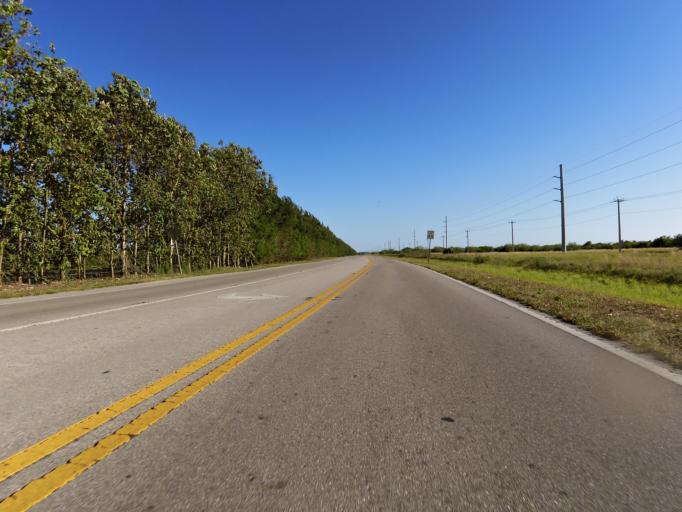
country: US
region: Florida
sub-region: Collier County
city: Immokalee
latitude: 26.3519
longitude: -81.4168
